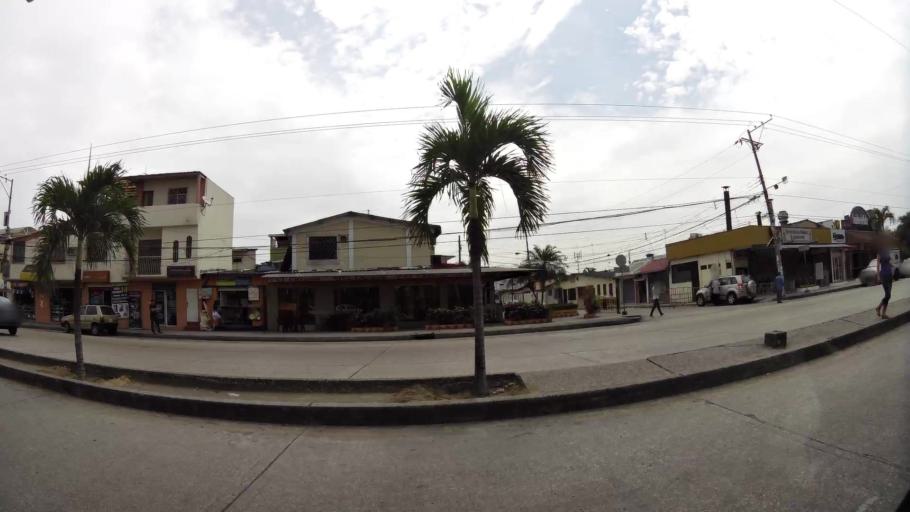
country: EC
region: Guayas
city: Eloy Alfaro
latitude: -2.1438
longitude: -79.8932
